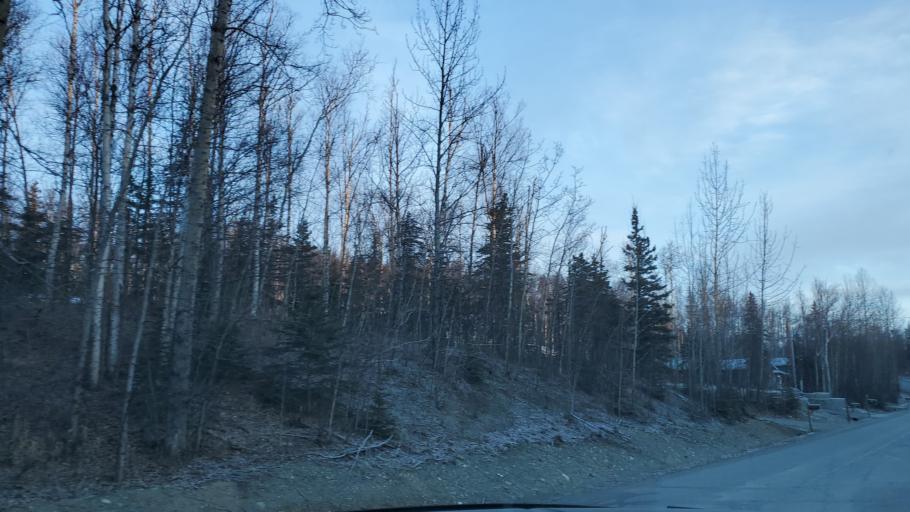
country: US
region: Alaska
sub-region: Matanuska-Susitna Borough
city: Lakes
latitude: 61.6041
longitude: -149.3194
